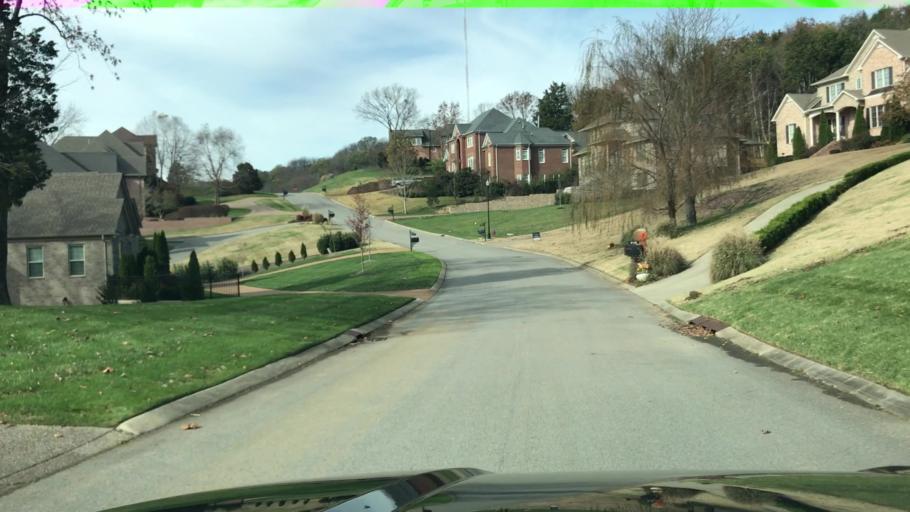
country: US
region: Tennessee
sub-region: Davidson County
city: Forest Hills
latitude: 36.0264
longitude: -86.8445
